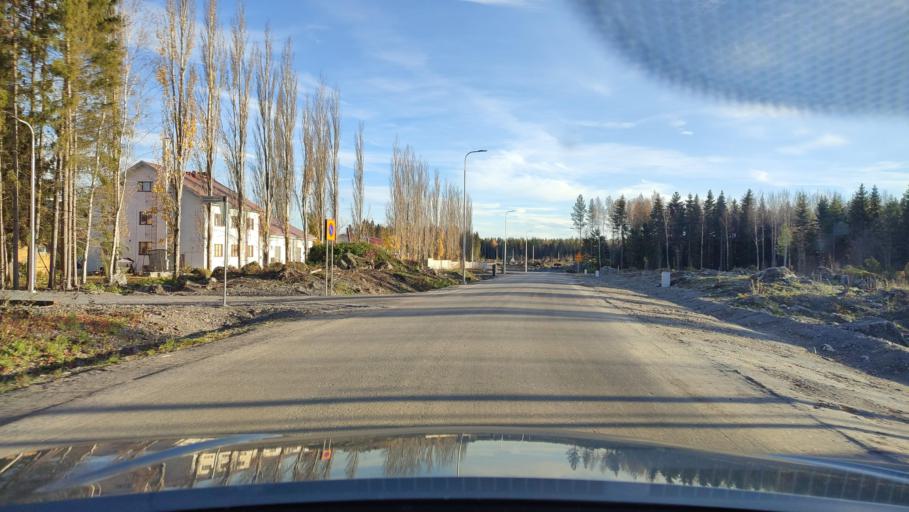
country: FI
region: Ostrobothnia
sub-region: Vaasa
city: Teeriniemi
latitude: 63.0664
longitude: 21.6985
